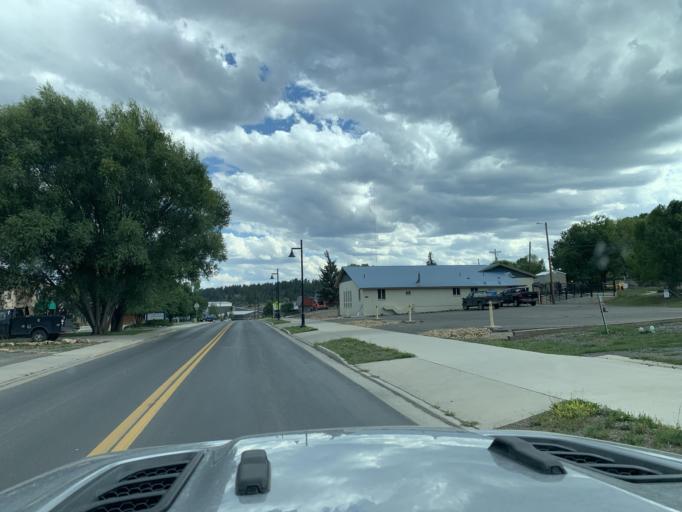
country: US
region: Colorado
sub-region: Archuleta County
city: Pagosa Springs
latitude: 37.2610
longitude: -107.0172
